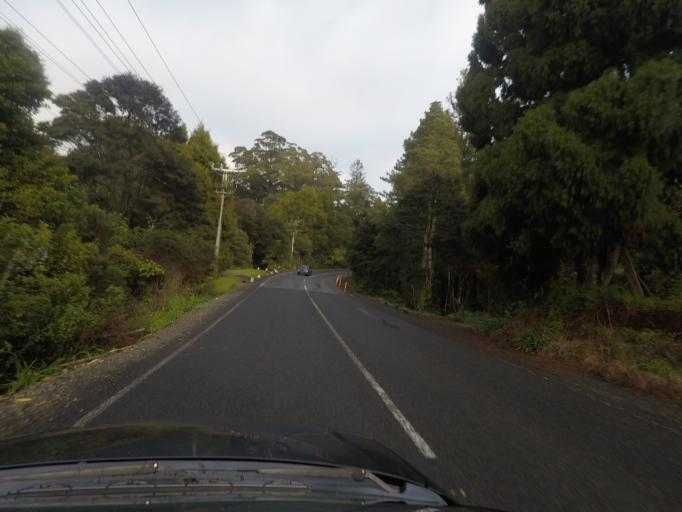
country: NZ
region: Auckland
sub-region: Auckland
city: Waitakere
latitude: -36.9174
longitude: 174.5917
